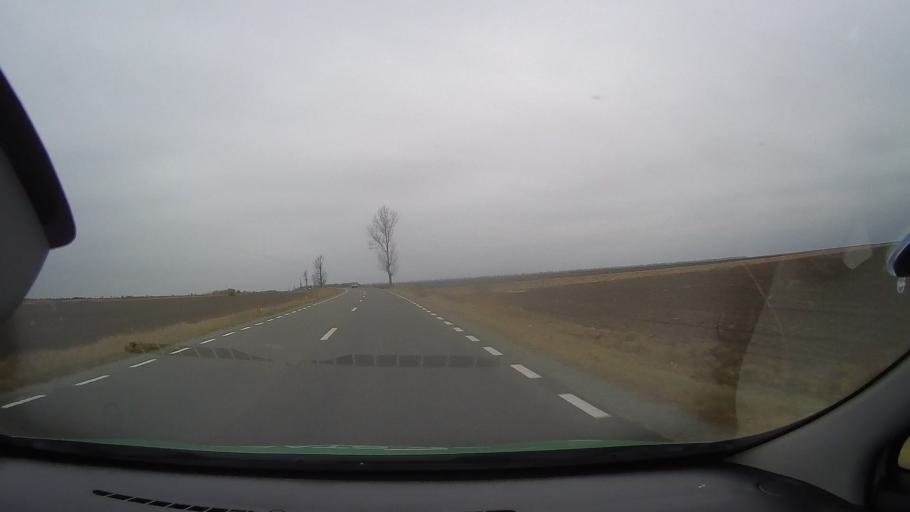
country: RO
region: Ialomita
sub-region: Comuna Scanteia
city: Iazu
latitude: 44.7159
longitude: 27.4197
